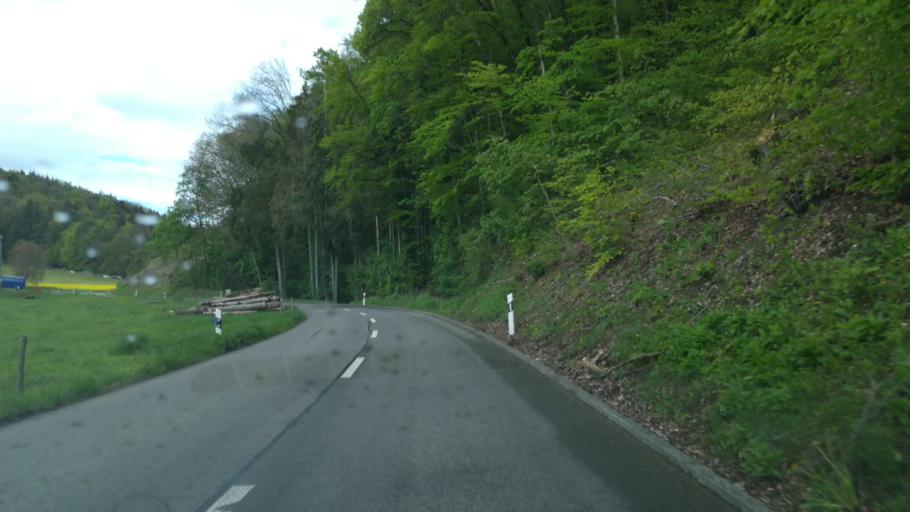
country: CH
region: Schaffhausen
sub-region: Bezirk Reiat
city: Stetten
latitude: 47.7337
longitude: 8.6391
